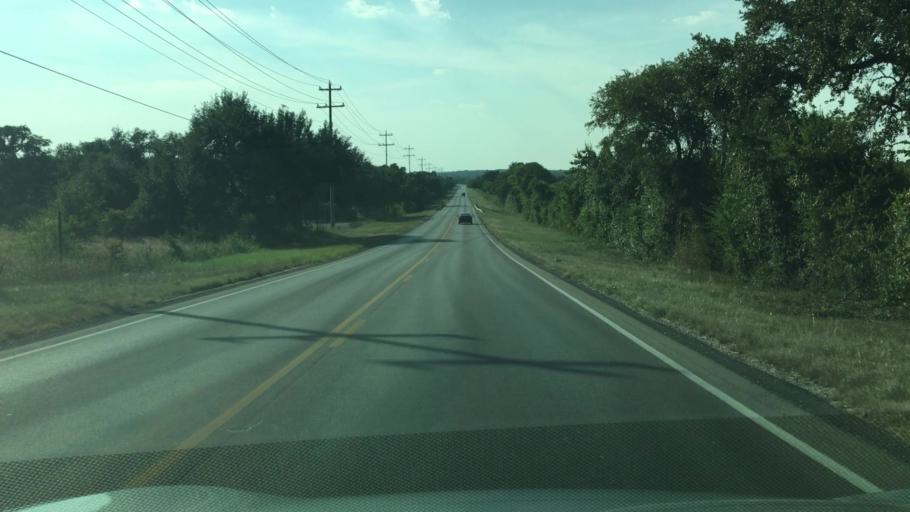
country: US
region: Texas
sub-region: Travis County
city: Shady Hollow
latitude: 30.1048
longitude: -97.9413
